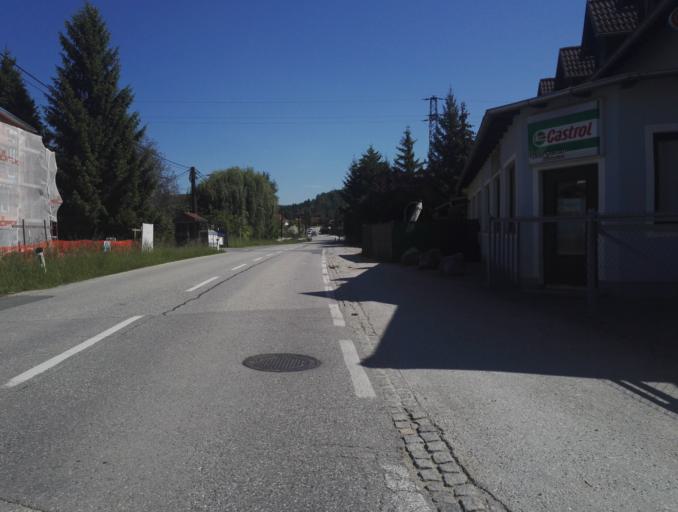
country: AT
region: Styria
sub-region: Politischer Bezirk Graz-Umgebung
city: Hart bei Graz
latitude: 47.0527
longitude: 15.5287
